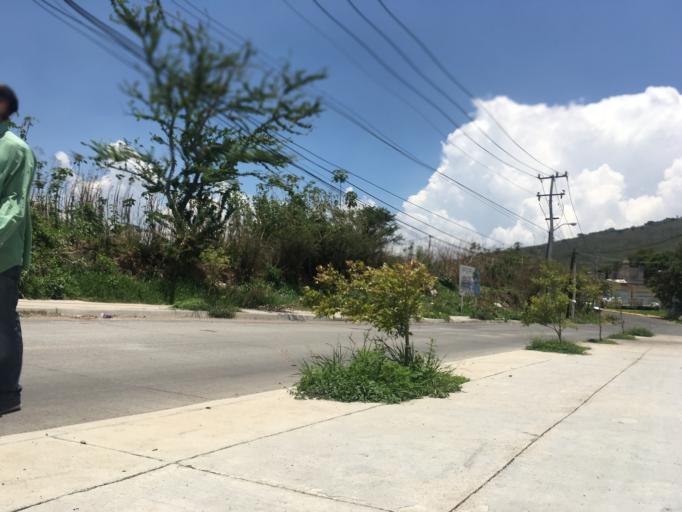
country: MX
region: Jalisco
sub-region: Tlajomulco de Zuniga
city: La Roca
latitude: 20.5148
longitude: -103.4260
